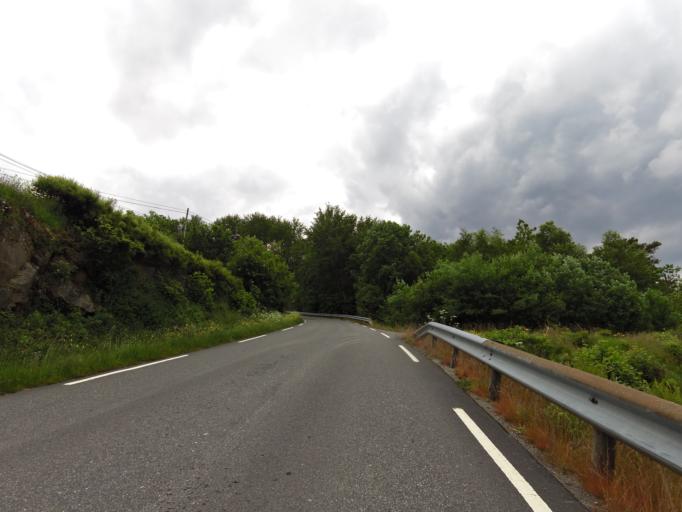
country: NO
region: Vest-Agder
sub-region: Lyngdal
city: Lyngdal
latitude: 58.1053
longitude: 6.9612
